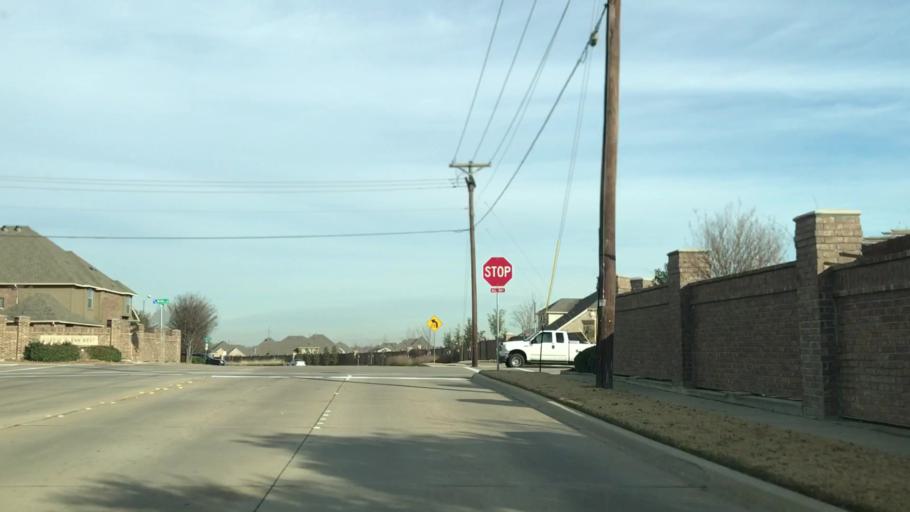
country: US
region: Texas
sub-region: Tarrant County
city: Watauga
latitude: 32.8928
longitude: -97.2119
